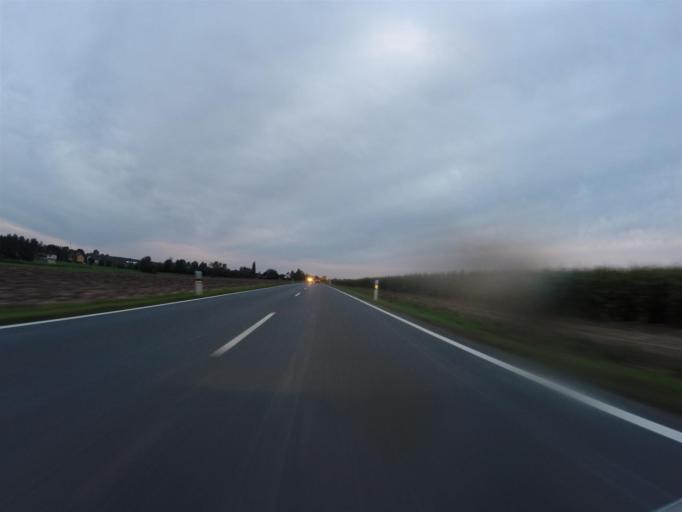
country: DE
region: Thuringia
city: Hainspitz
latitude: 50.9581
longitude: 11.8270
